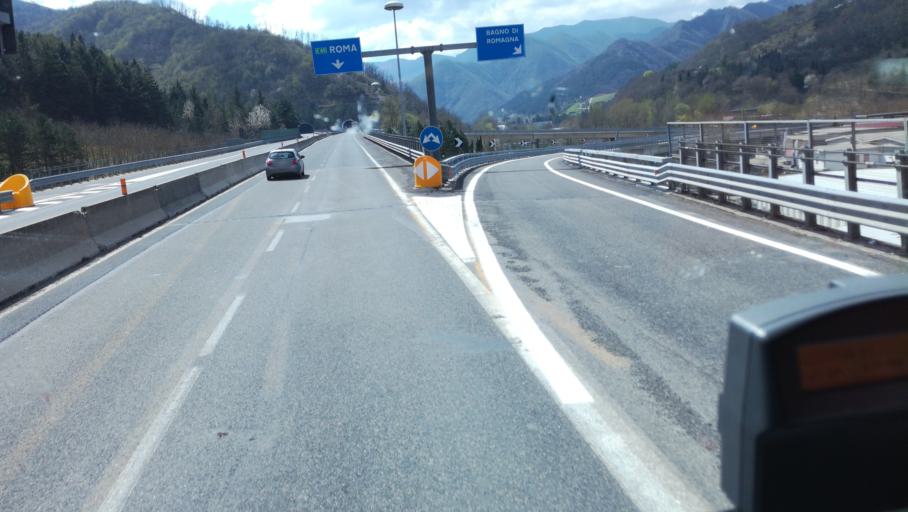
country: IT
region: Emilia-Romagna
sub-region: Forli-Cesena
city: San Piero in Bagno
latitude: 43.8471
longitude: 11.9752
